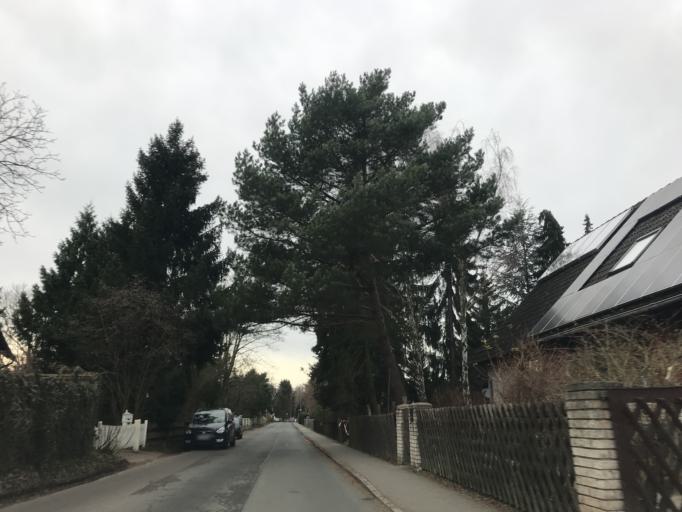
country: DE
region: Berlin
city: Kladow
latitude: 52.4523
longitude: 13.1369
